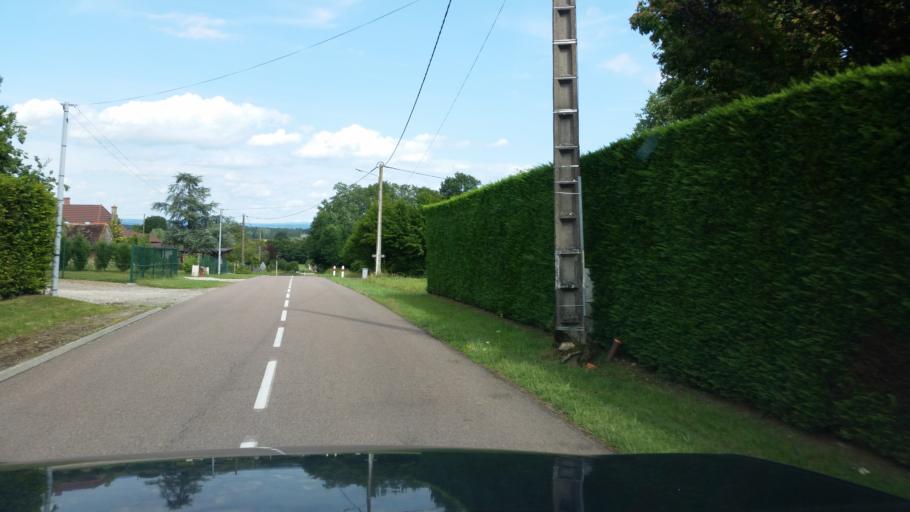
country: FR
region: Bourgogne
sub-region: Departement de Saone-et-Loire
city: Saint-Germain-du-Bois
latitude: 46.7319
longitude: 5.2775
